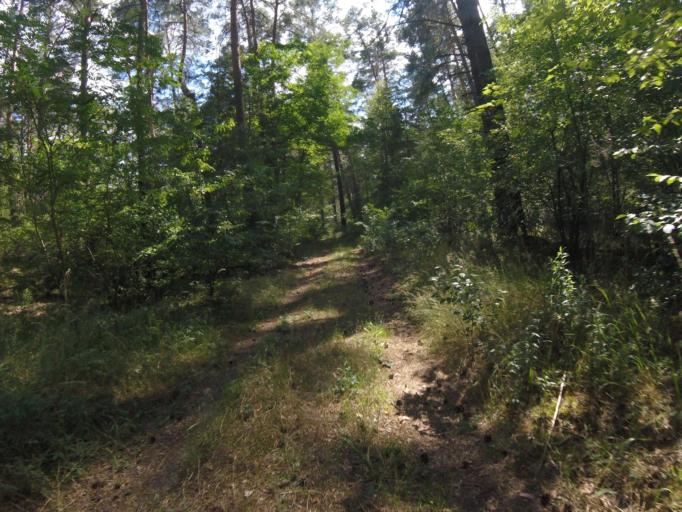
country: DE
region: Brandenburg
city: Wildau
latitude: 52.3296
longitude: 13.6748
